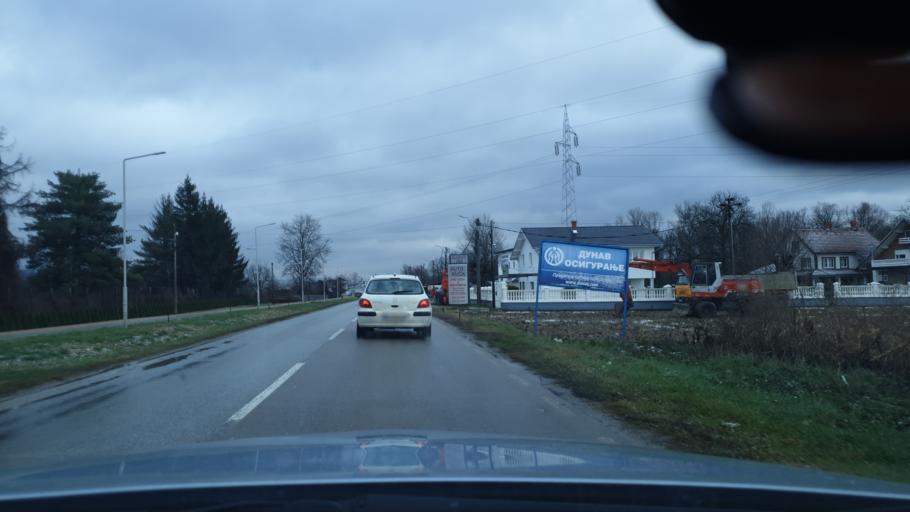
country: RS
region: Central Serbia
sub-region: Branicevski Okrug
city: Petrovac
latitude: 44.3949
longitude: 21.4049
